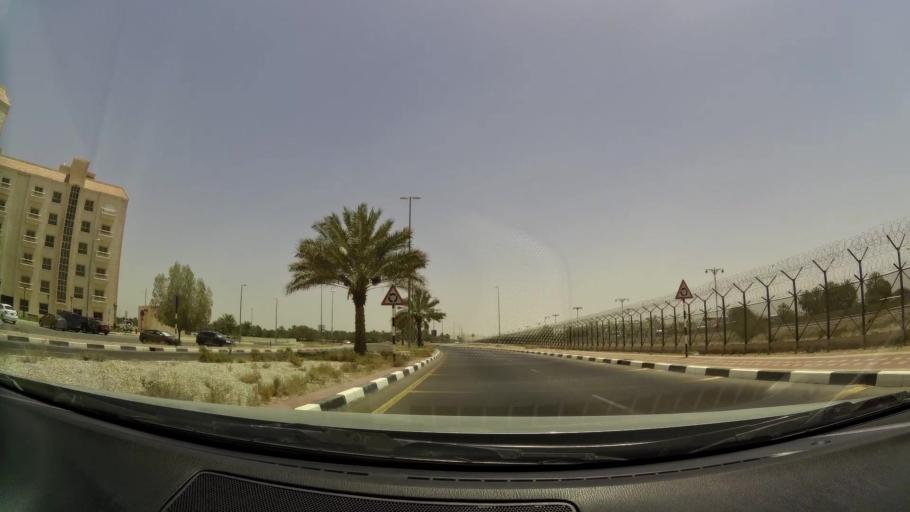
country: OM
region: Al Buraimi
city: Al Buraymi
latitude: 24.2720
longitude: 55.7816
